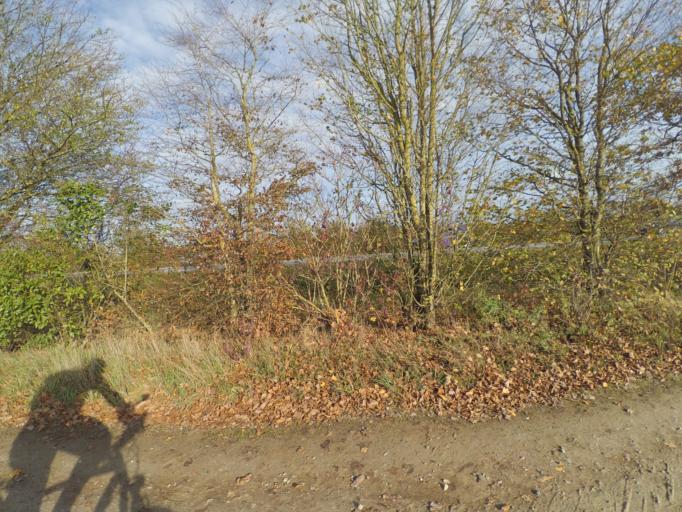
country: FR
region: Pays de la Loire
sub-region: Departement de la Vendee
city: Saint-Hilaire-de-Loulay
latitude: 47.0187
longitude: -1.3443
